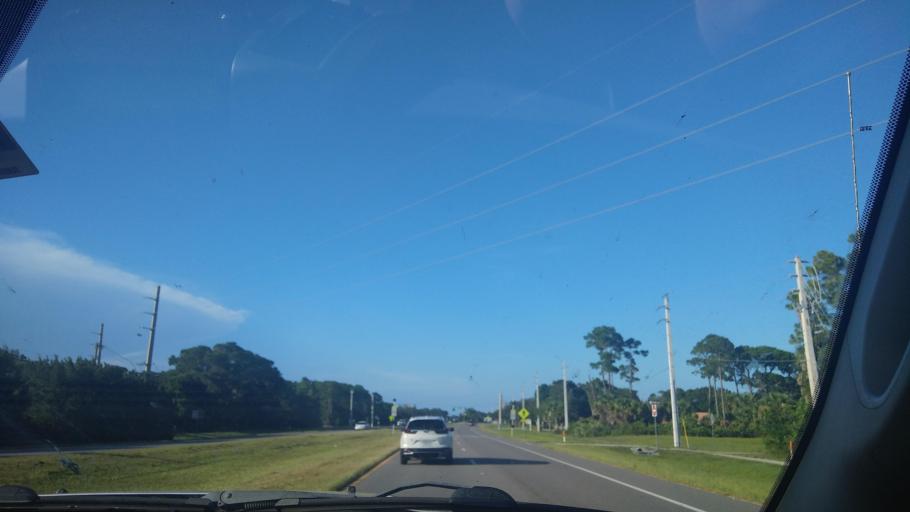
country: US
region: Florida
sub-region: Indian River County
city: Sebastian
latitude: 27.8000
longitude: -80.4786
